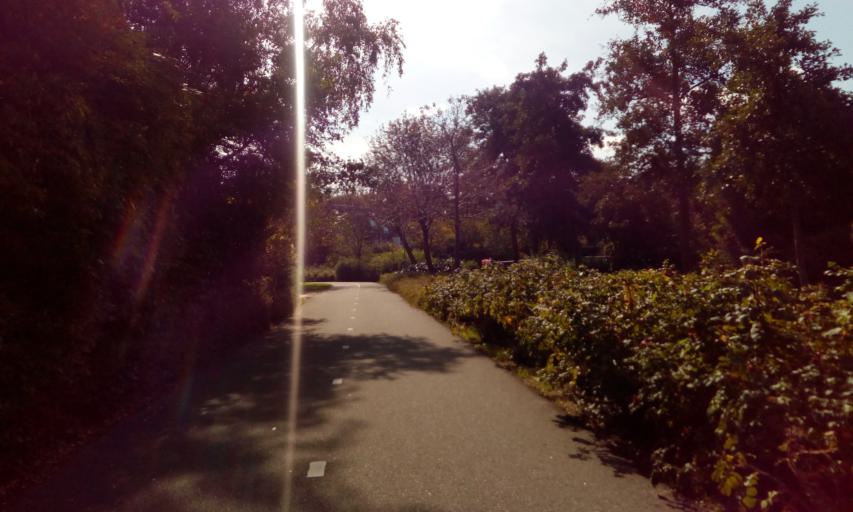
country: NL
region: South Holland
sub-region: Gemeente Voorschoten
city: Voorschoten
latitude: 52.1428
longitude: 4.4549
